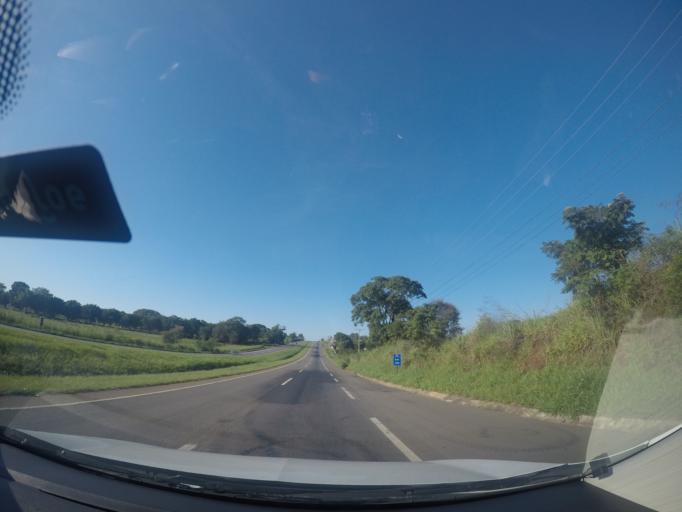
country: BR
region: Goias
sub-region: Aparecida De Goiania
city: Aparecida de Goiania
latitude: -16.8580
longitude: -49.2487
